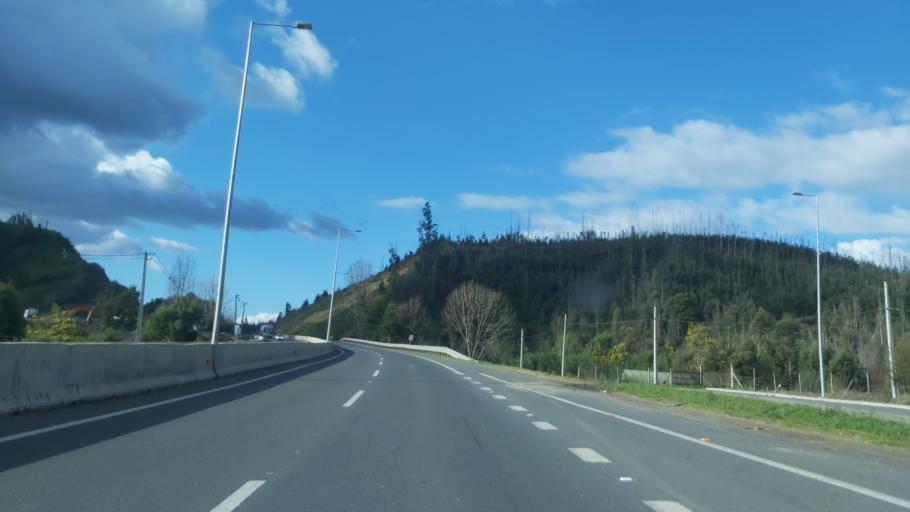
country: CL
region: Biobio
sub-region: Provincia de Concepcion
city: Penco
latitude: -36.8127
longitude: -72.9766
